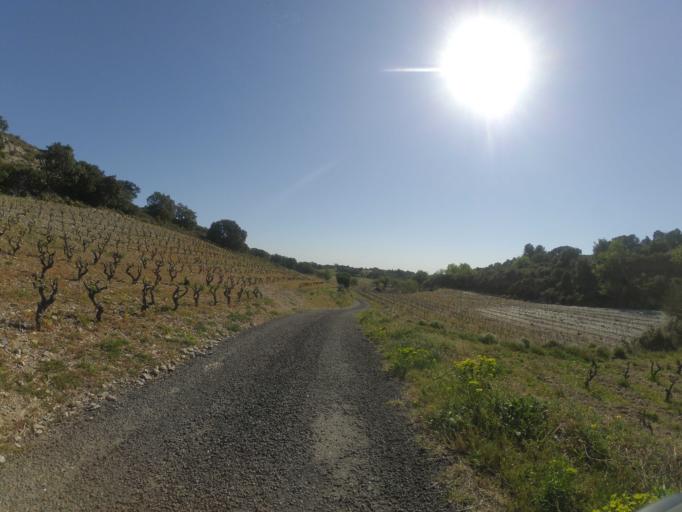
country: FR
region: Languedoc-Roussillon
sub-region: Departement des Pyrenees-Orientales
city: Baixas
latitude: 42.7607
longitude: 2.7690
